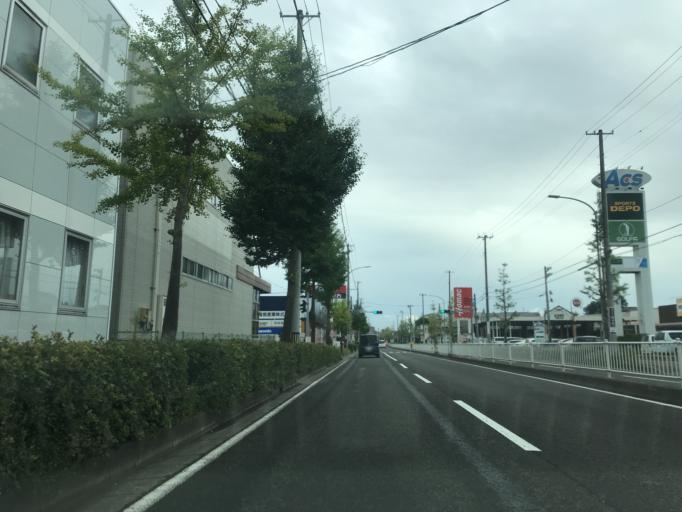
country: JP
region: Miyagi
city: Sendai-shi
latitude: 38.3161
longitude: 140.8729
